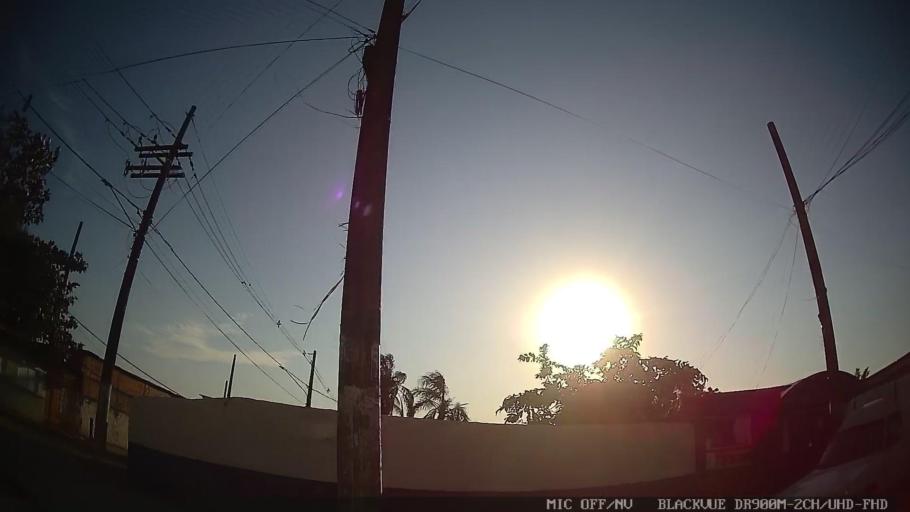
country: BR
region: Sao Paulo
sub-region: Guaruja
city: Guaruja
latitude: -23.9811
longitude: -46.2617
